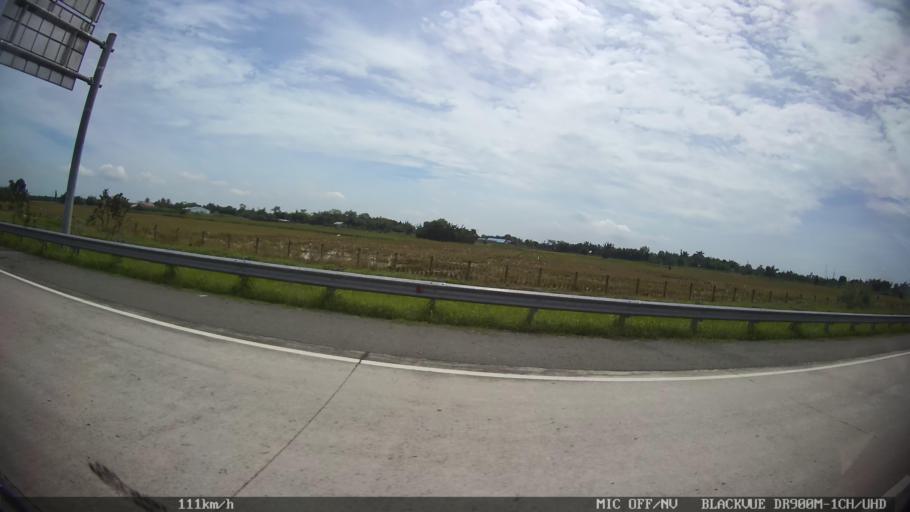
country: ID
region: North Sumatra
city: Percut
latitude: 3.5682
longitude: 98.8485
